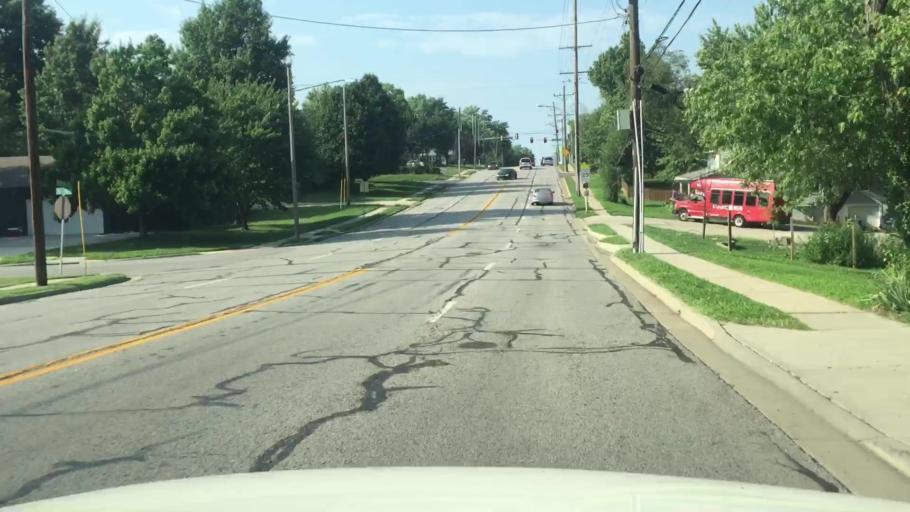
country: US
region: Kansas
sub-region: Johnson County
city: Shawnee
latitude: 39.0373
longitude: -94.7145
